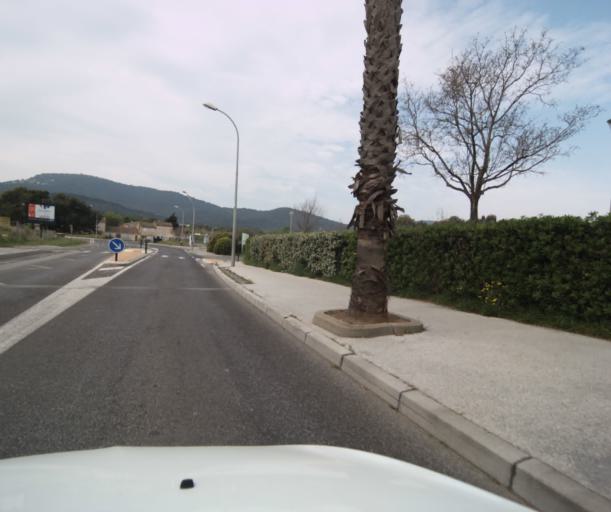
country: FR
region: Provence-Alpes-Cote d'Azur
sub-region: Departement du Var
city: Hyeres
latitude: 43.1185
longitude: 6.1135
